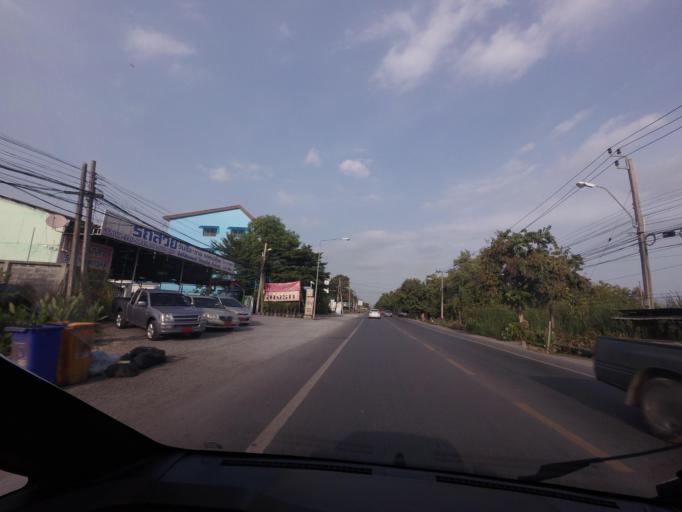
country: TH
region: Bangkok
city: Nong Chok
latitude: 13.8534
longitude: 100.8715
